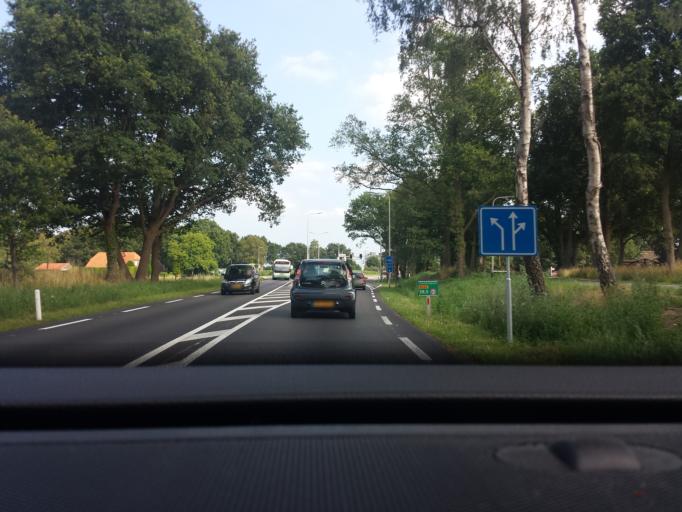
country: NL
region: Gelderland
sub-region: Gemeente Lochem
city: Lochem
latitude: 52.1748
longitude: 6.3877
